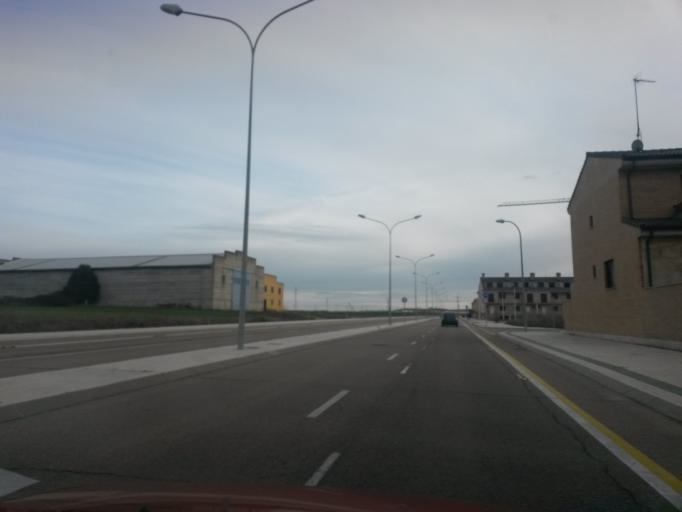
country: ES
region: Castille and Leon
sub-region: Provincia de Salamanca
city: Villares de la Reina
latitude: 41.0083
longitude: -5.6438
